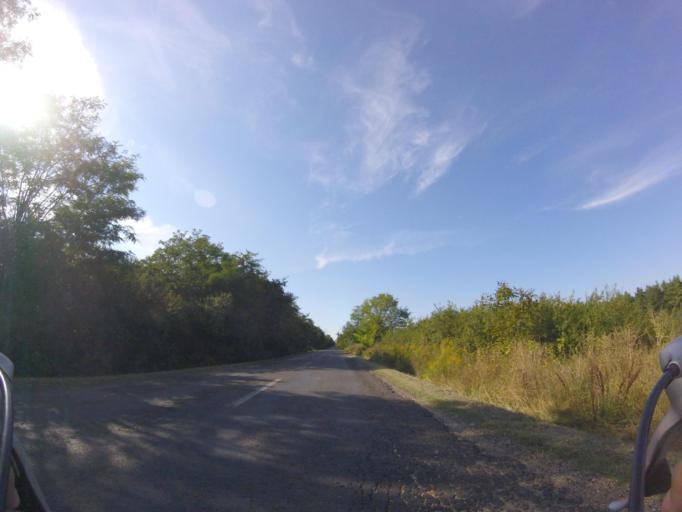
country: HU
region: Pest
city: Gomba
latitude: 47.3794
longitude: 19.5133
